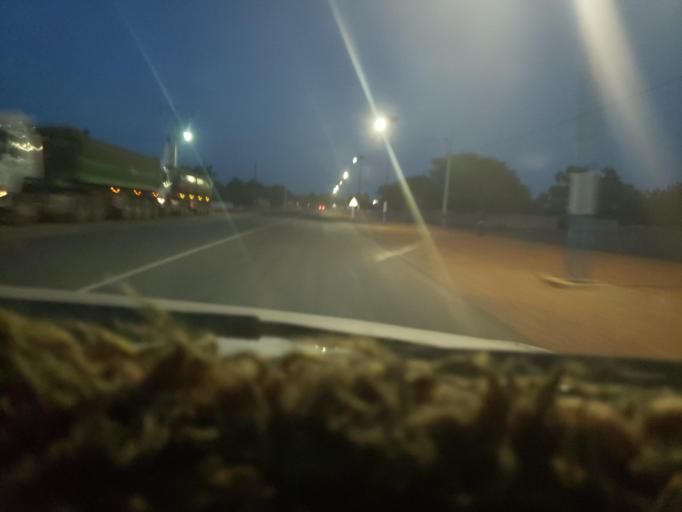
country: SN
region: Louga
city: Ndibene Dahra
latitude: 15.3835
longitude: -15.2399
